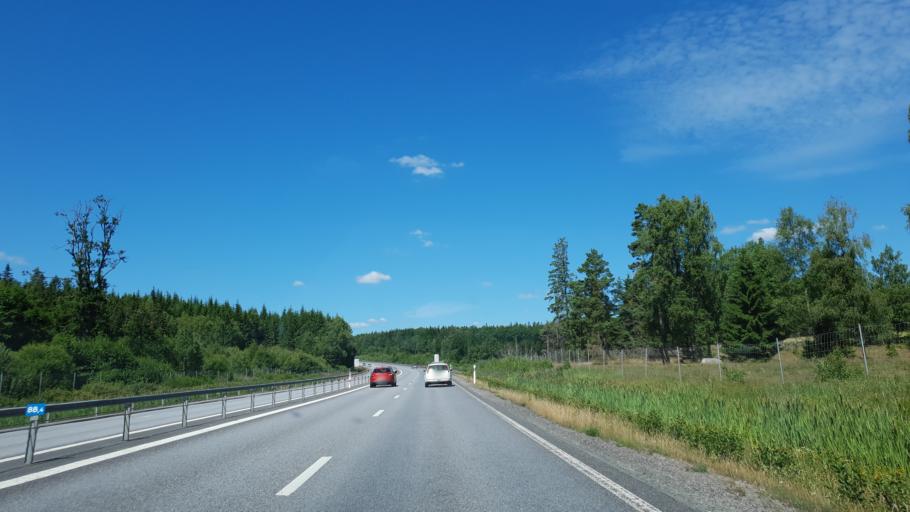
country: SE
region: Kronoberg
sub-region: Vaxjo Kommun
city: Gemla
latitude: 56.9180
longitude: 14.6150
